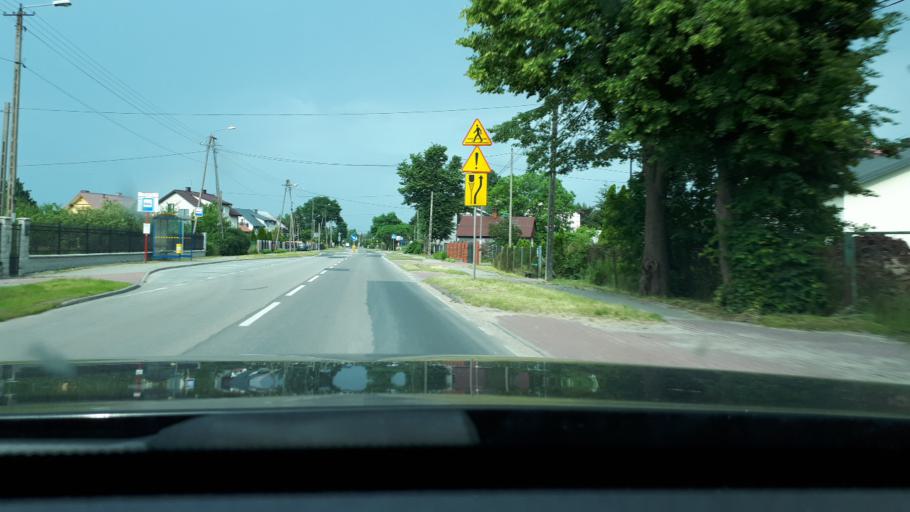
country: PL
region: Masovian Voivodeship
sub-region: Powiat warszawski zachodni
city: Leszno
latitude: 52.2603
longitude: 20.6130
